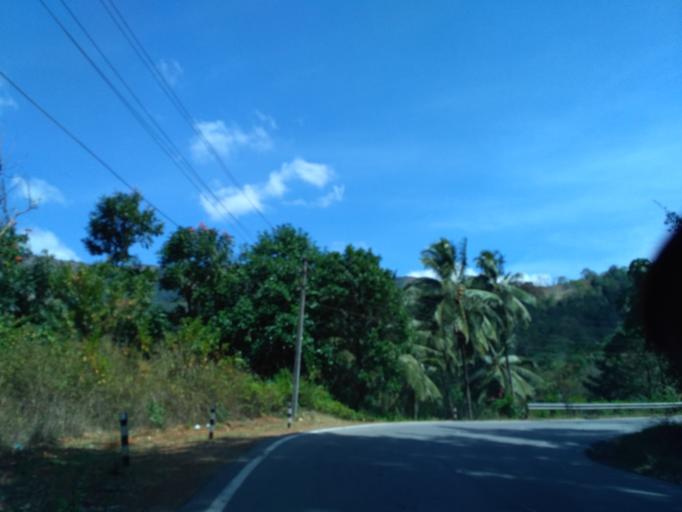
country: IN
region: Karnataka
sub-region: Kodagu
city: Madikeri
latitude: 12.4422
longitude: 75.6498
